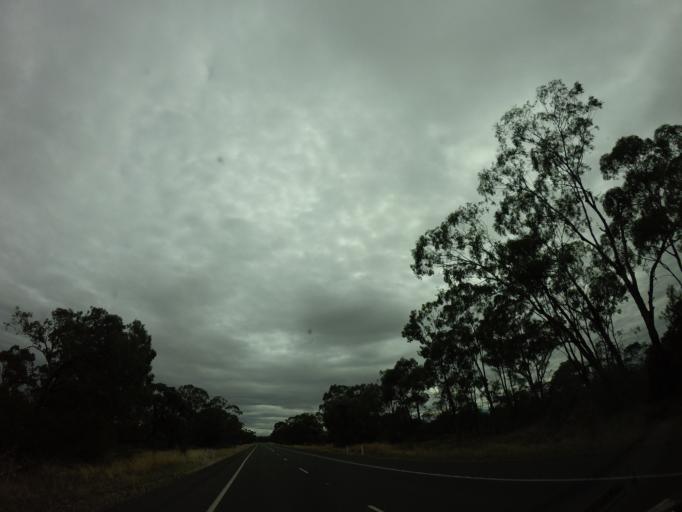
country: AU
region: New South Wales
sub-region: Narrabri
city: Narrabri
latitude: -30.3592
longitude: 149.7418
